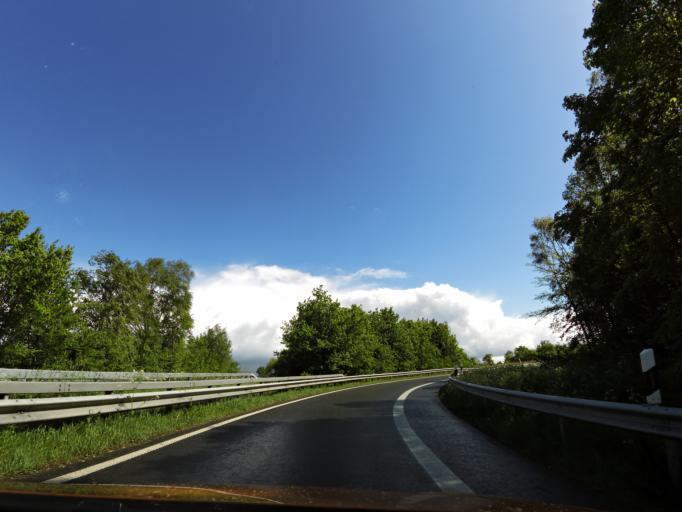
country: DE
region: Lower Saxony
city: Oldenburg
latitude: 53.1657
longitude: 8.2692
